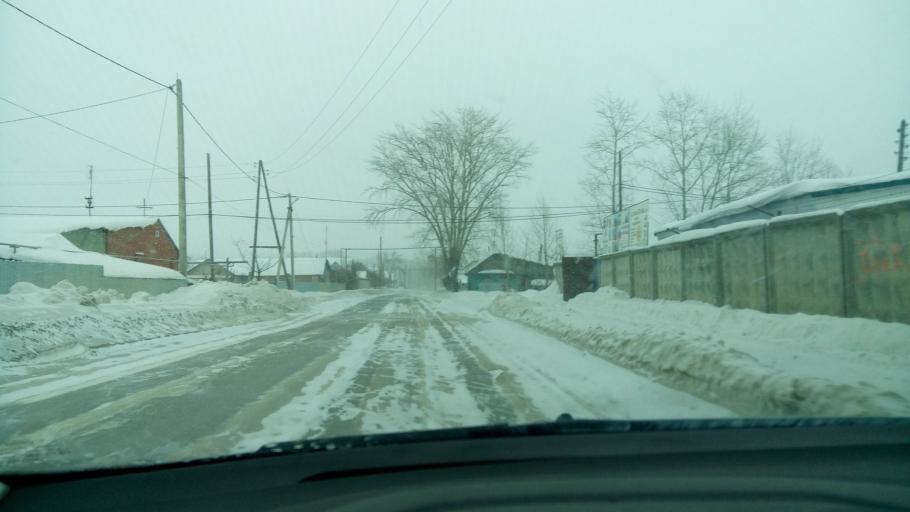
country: RU
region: Sverdlovsk
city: Bogdanovich
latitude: 56.7805
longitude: 62.0327
